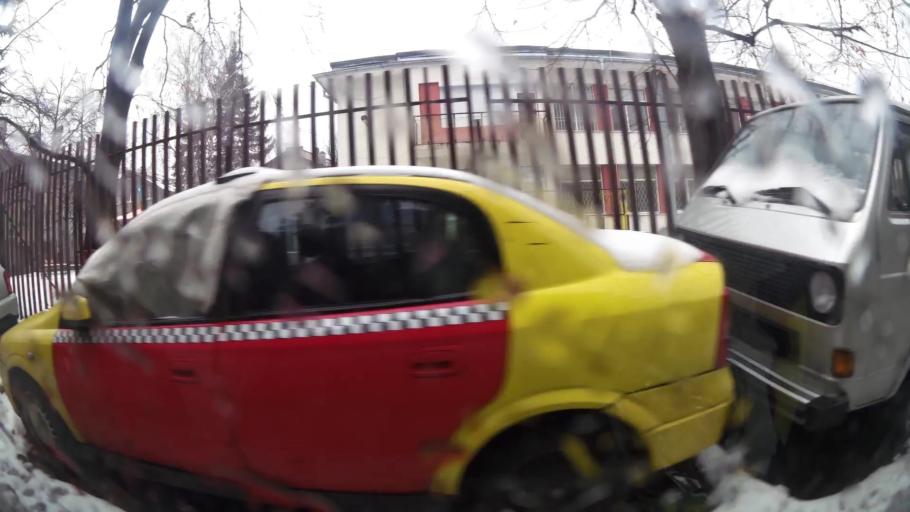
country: BG
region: Sofia-Capital
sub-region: Stolichna Obshtina
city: Sofia
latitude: 42.6805
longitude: 23.2642
